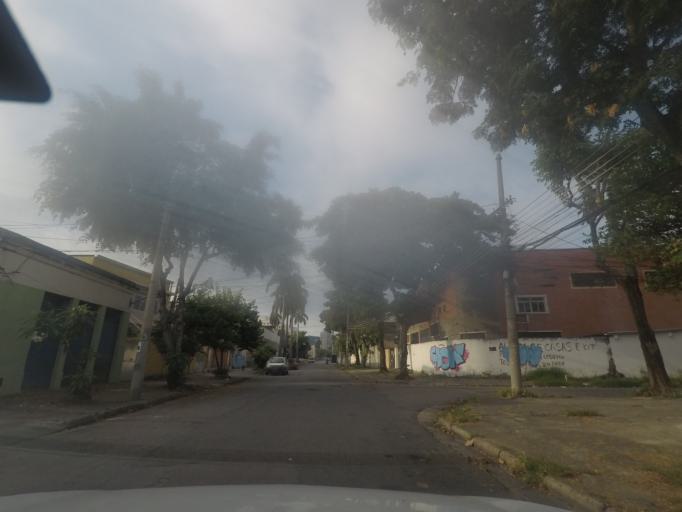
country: BR
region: Rio de Janeiro
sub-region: Duque De Caxias
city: Duque de Caxias
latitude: -22.8354
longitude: -43.2737
